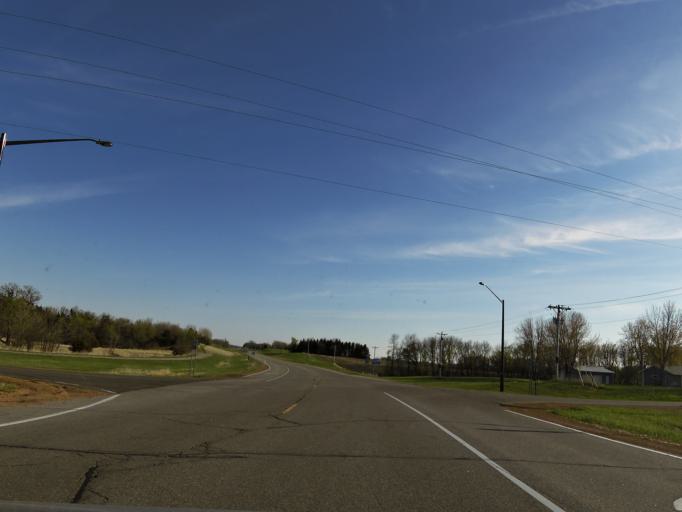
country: US
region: Minnesota
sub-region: Le Sueur County
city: New Prague
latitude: 44.5913
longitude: -93.5067
